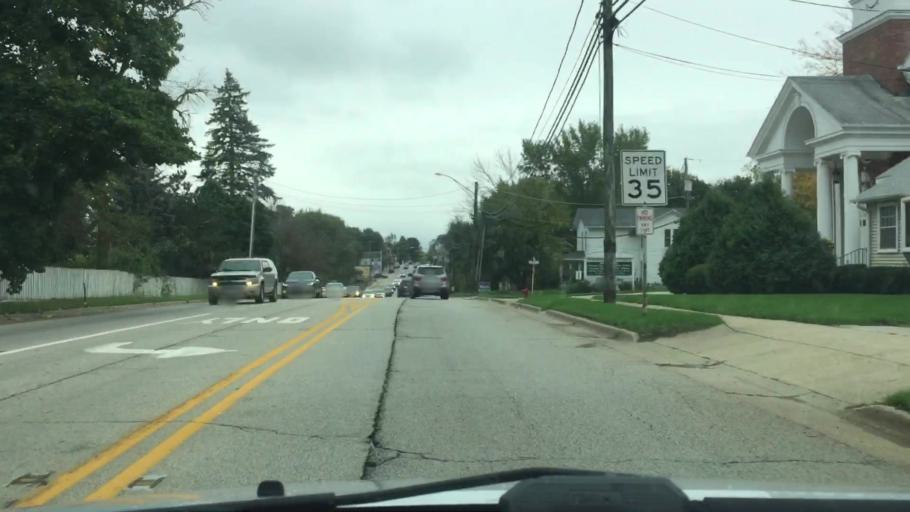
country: US
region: Illinois
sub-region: McHenry County
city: Richmond
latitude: 42.4794
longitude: -88.3061
